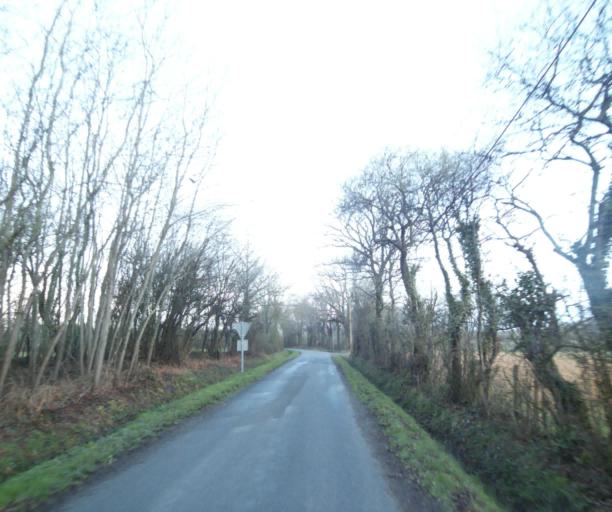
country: FR
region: Pays de la Loire
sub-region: Departement de la Loire-Atlantique
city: Malville
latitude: 47.3843
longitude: -1.8948
